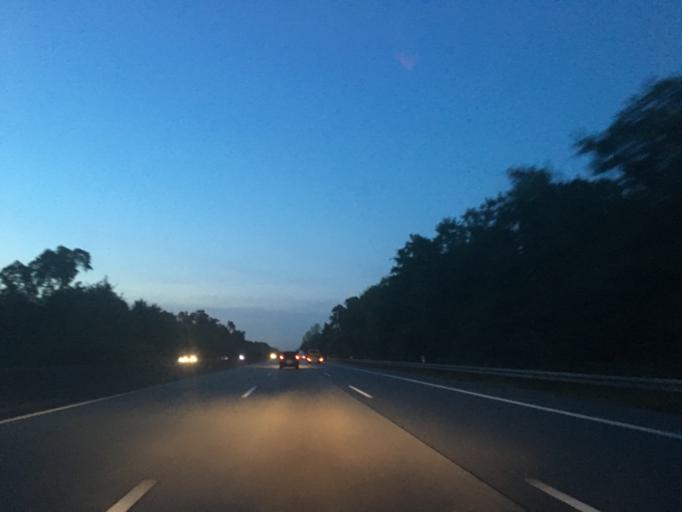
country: DE
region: Hesse
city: Lorsch
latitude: 49.6000
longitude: 8.5596
